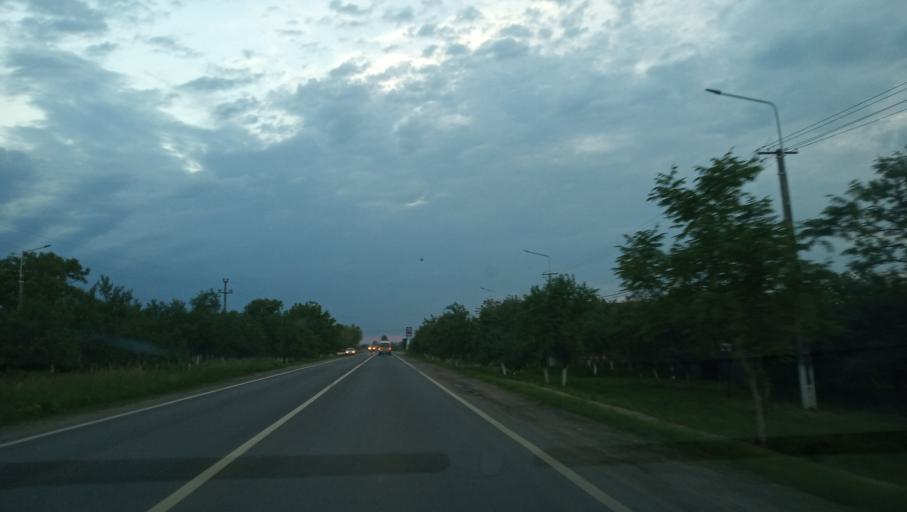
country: RO
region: Timis
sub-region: Comuna Jebel
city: Jebel
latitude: 45.5688
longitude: 21.2076
